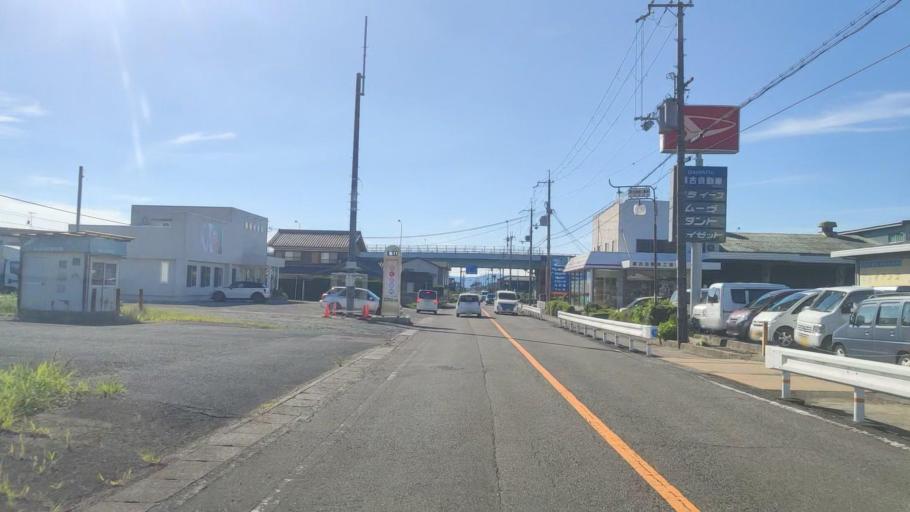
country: JP
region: Shiga Prefecture
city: Minakuchicho-matoba
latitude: 34.8918
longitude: 136.2277
